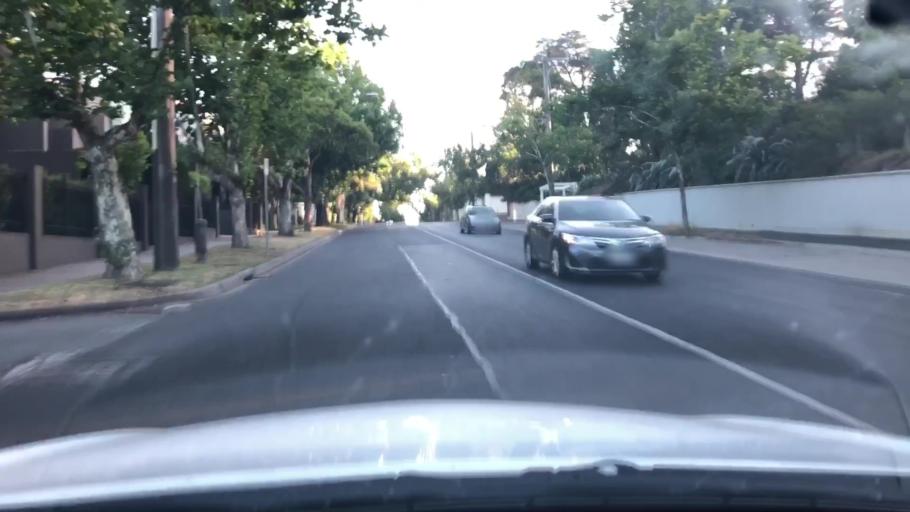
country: AU
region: Victoria
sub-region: Stonnington
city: Toorak
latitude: -37.8378
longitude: 145.0052
